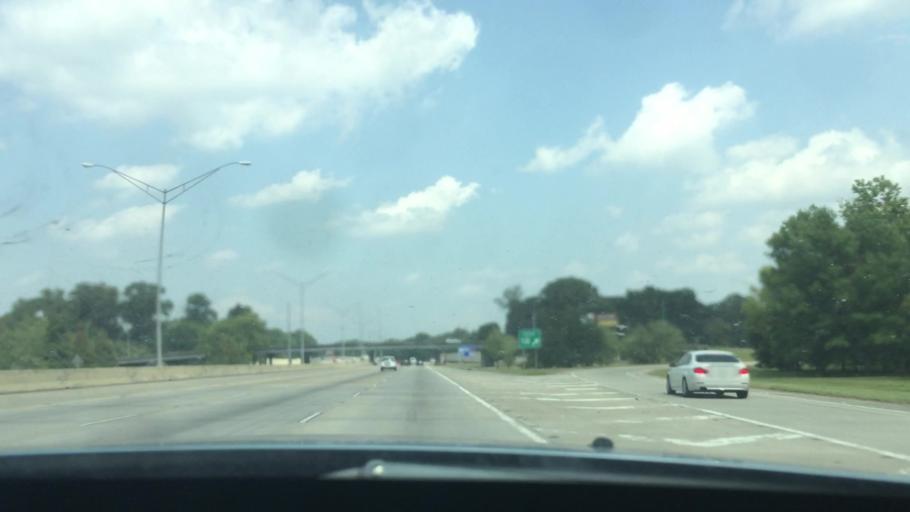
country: US
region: Louisiana
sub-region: East Baton Rouge Parish
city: Westminster
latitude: 30.4173
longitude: -91.1007
